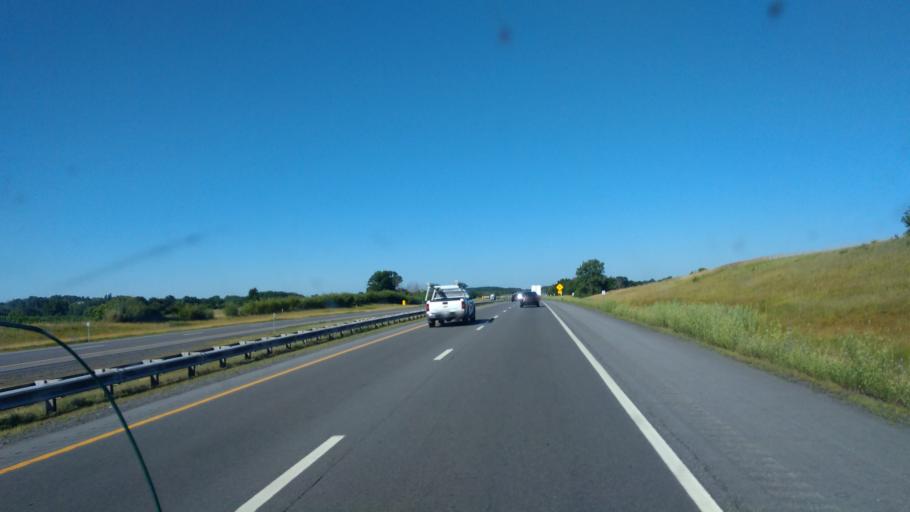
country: US
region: New York
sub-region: Monroe County
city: Scottsville
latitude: 43.0399
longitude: -77.8017
